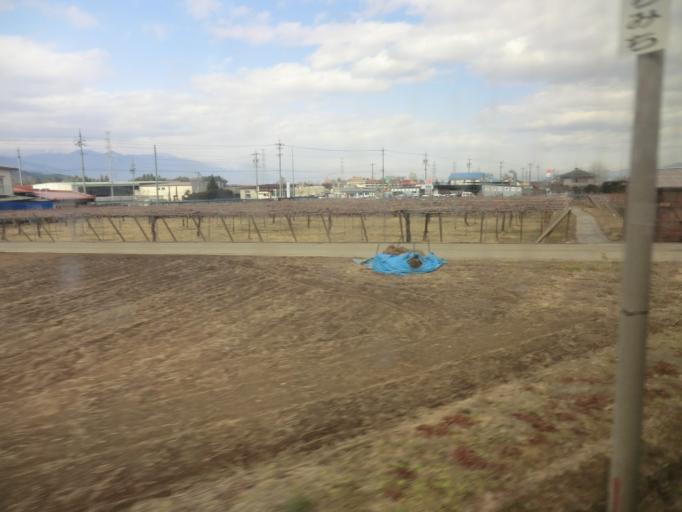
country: JP
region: Nagano
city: Shiojiri
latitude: 36.0969
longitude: 137.9279
